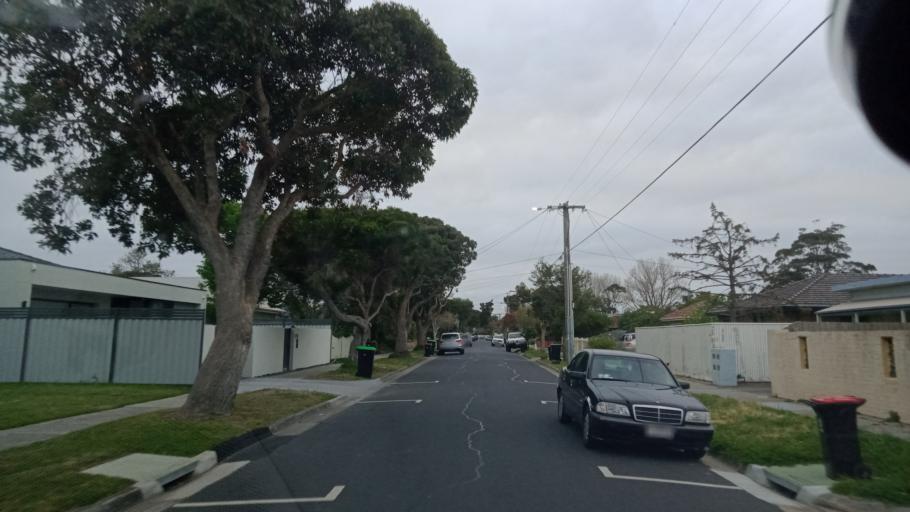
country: AU
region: Victoria
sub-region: Kingston
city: Edithvale
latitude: -38.0341
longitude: 145.1096
